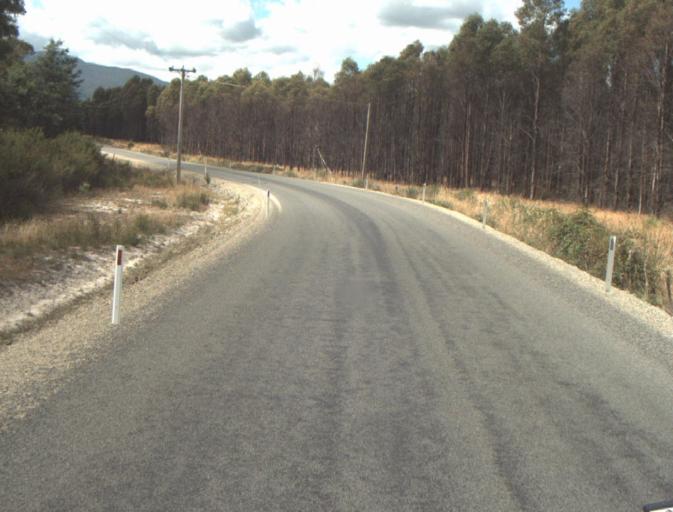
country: AU
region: Tasmania
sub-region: Launceston
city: Mayfield
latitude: -41.2136
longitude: 147.1902
